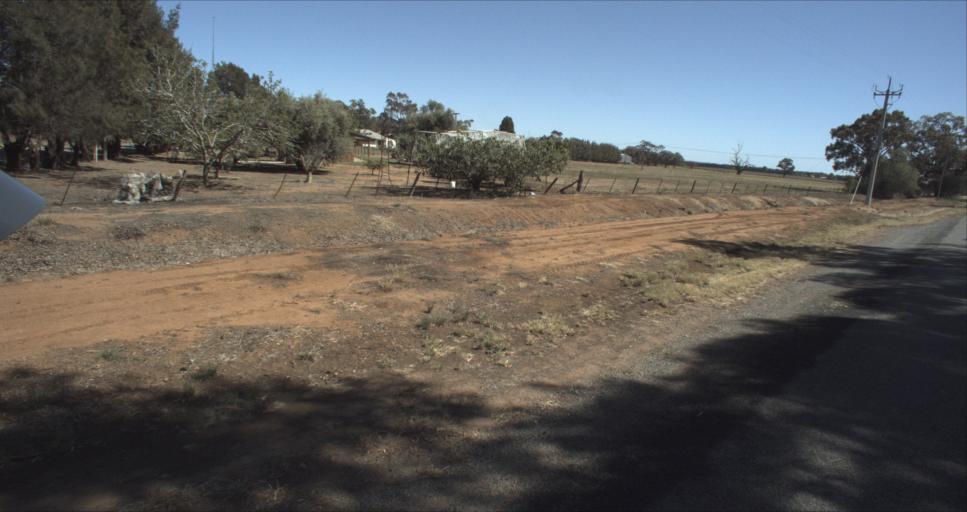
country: AU
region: New South Wales
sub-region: Leeton
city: Leeton
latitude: -34.5449
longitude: 146.3158
